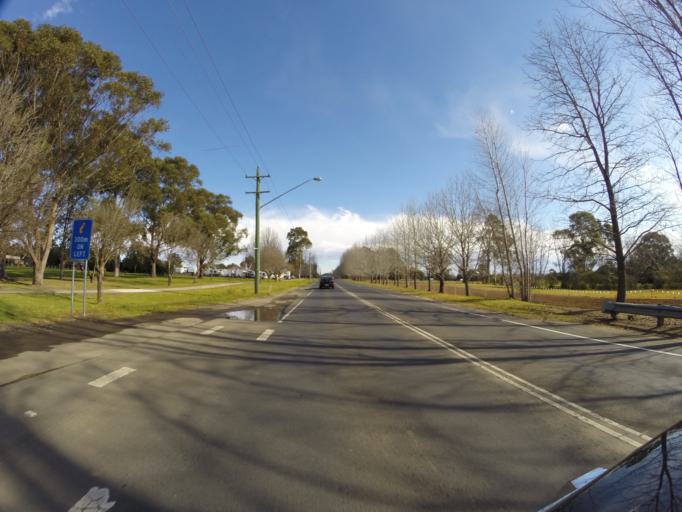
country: AU
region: New South Wales
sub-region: Camden
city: Elderslie
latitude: -34.0505
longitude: 150.7130
